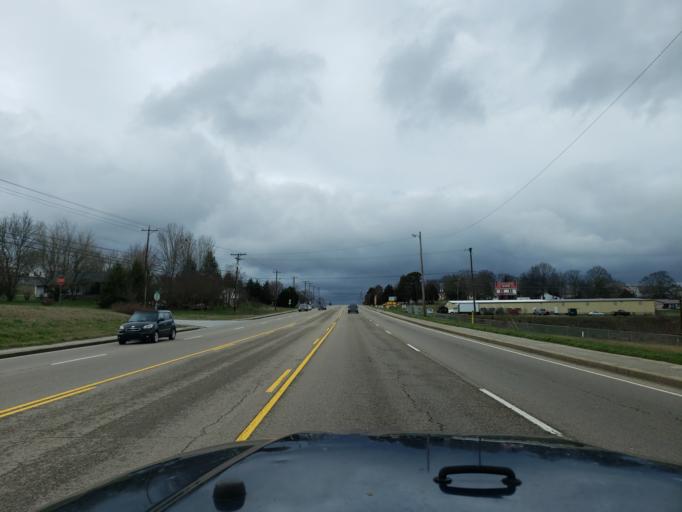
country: US
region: Tennessee
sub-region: Jefferson County
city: Jefferson City
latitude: 36.0994
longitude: -83.4818
